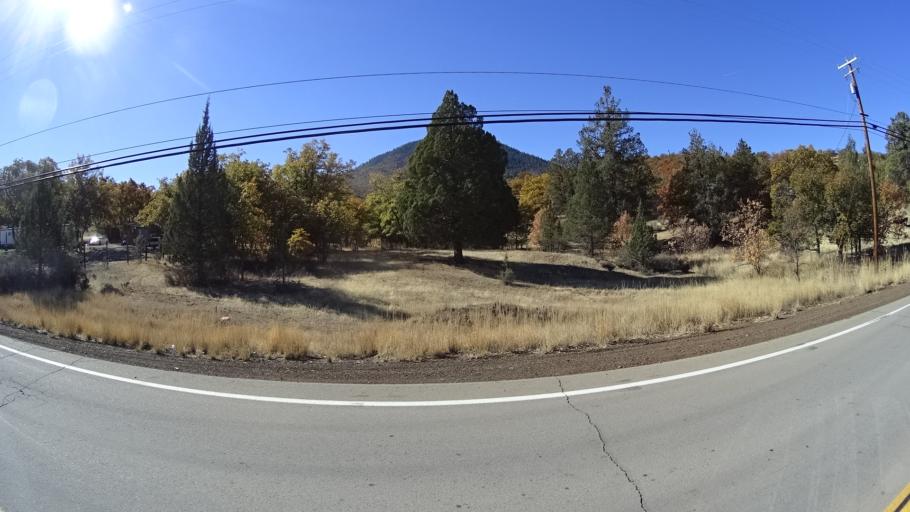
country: US
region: California
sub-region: Siskiyou County
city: Montague
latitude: 41.8871
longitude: -122.4910
